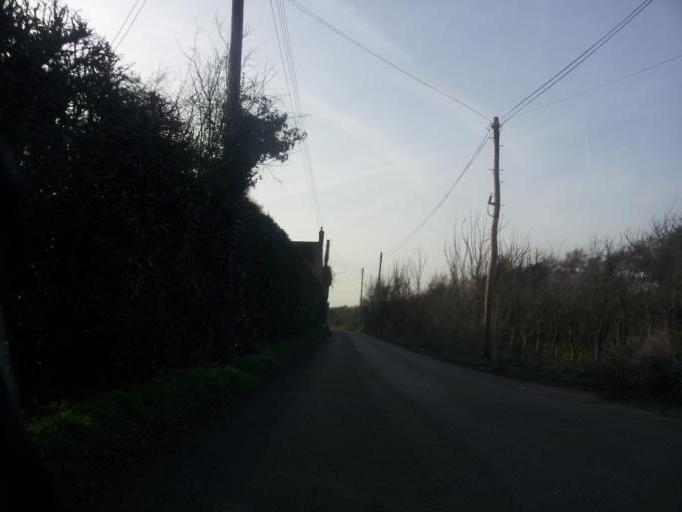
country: GB
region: England
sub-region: Kent
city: Teynham
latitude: 51.3359
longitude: 0.7972
